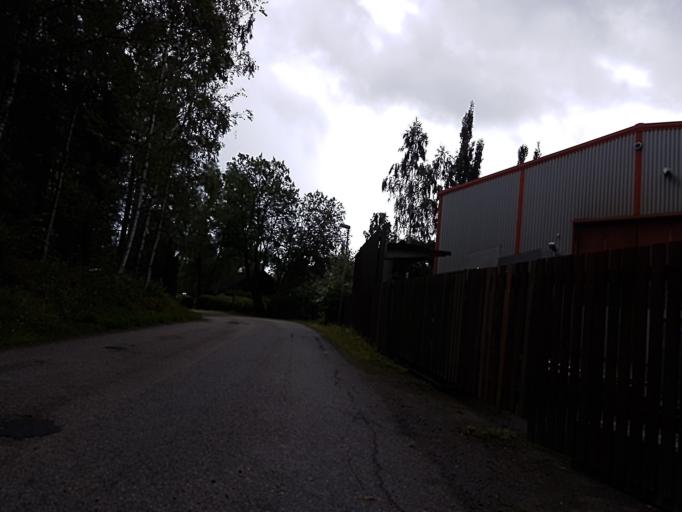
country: FI
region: Pirkanmaa
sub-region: Etelae-Pirkanmaa
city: Valkeakoski
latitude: 61.2533
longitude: 24.0488
